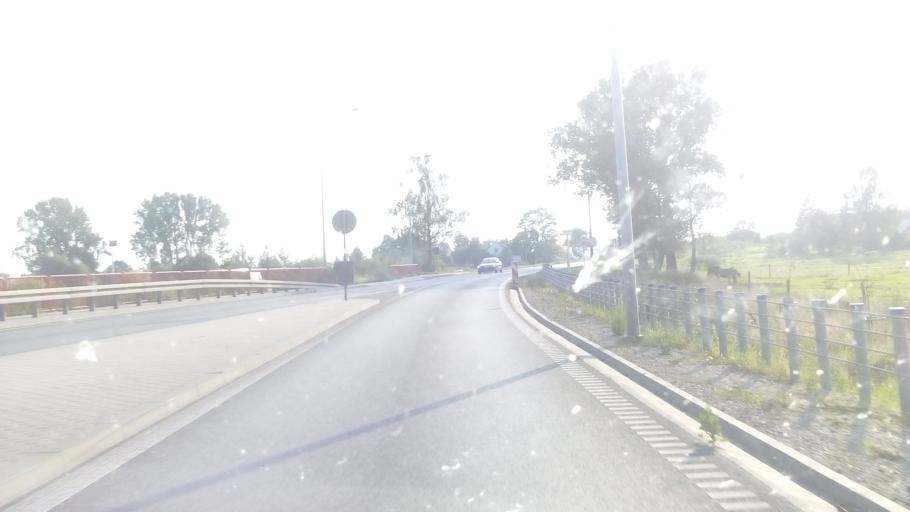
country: PL
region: Podlasie
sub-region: Powiat augustowski
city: Augustow
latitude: 53.8301
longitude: 22.9560
